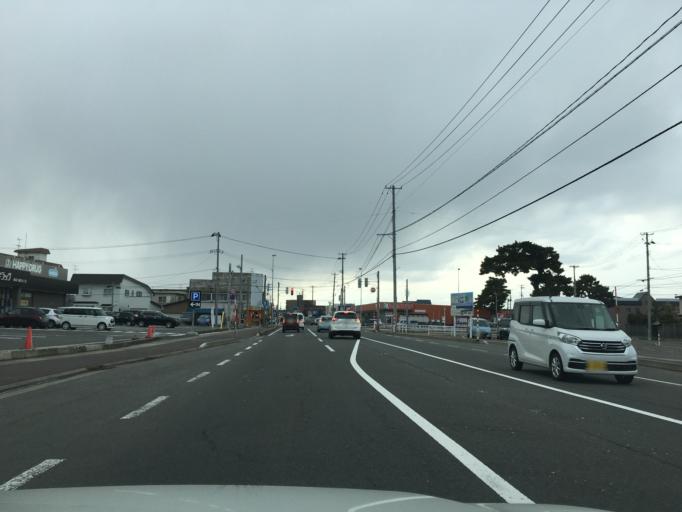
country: JP
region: Aomori
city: Aomori Shi
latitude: 40.8322
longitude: 140.7899
